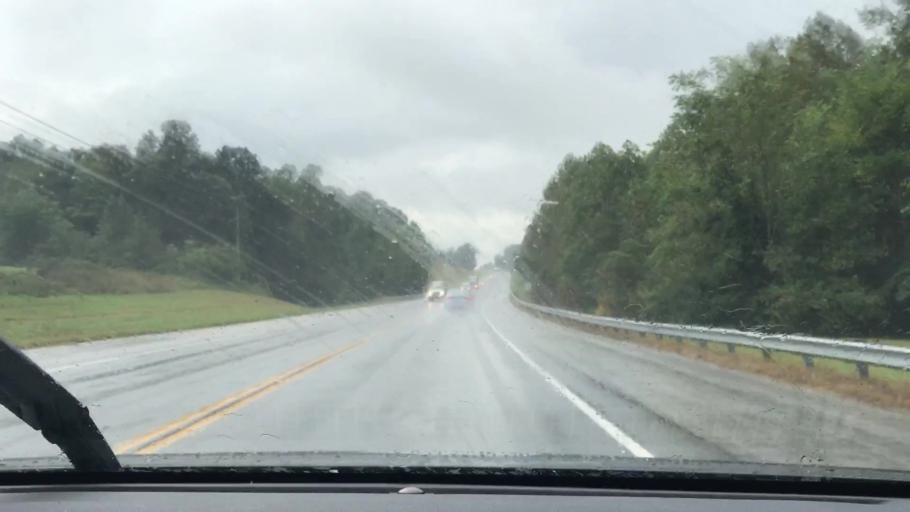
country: US
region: Tennessee
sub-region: Macon County
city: Lafayette
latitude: 36.5328
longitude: -86.0816
